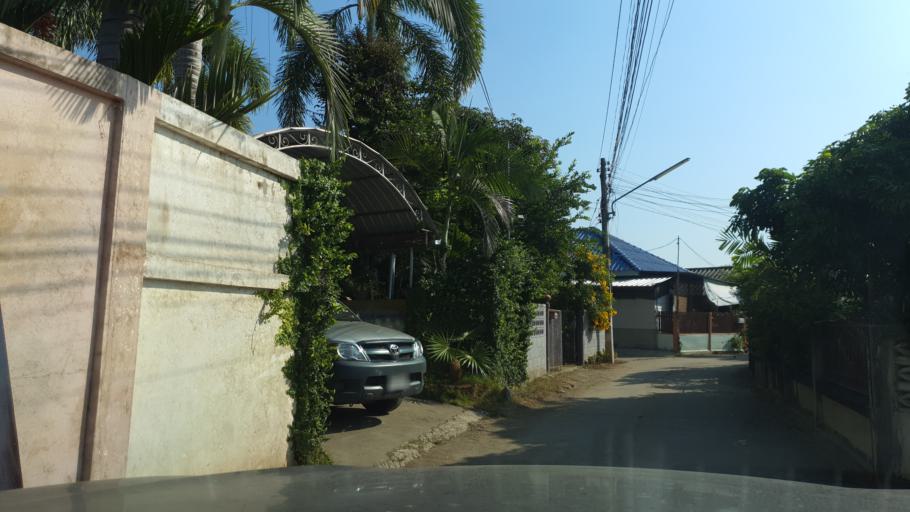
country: TH
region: Chiang Mai
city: Hang Dong
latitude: 18.7275
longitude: 98.9409
